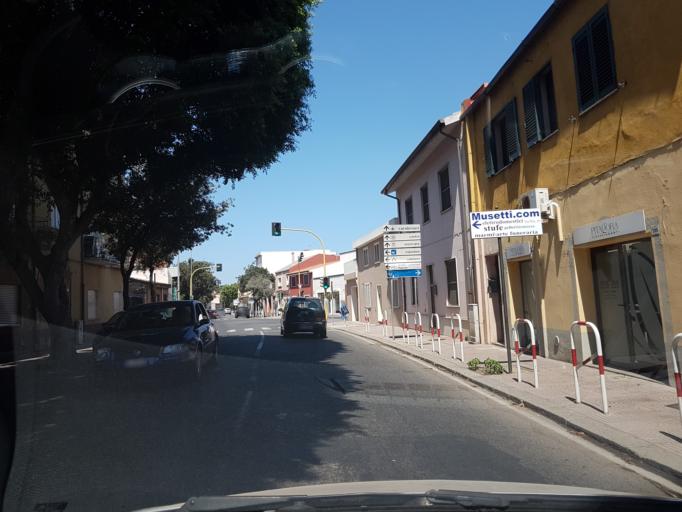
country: IT
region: Sardinia
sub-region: Provincia di Oristano
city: Oristano
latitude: 39.8984
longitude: 8.5943
